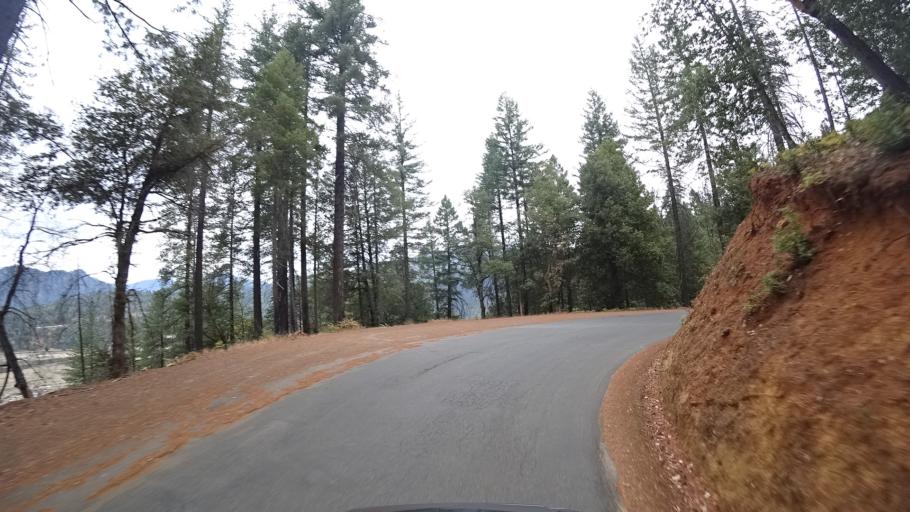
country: US
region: California
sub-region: Siskiyou County
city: Happy Camp
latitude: 41.7977
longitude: -123.3625
